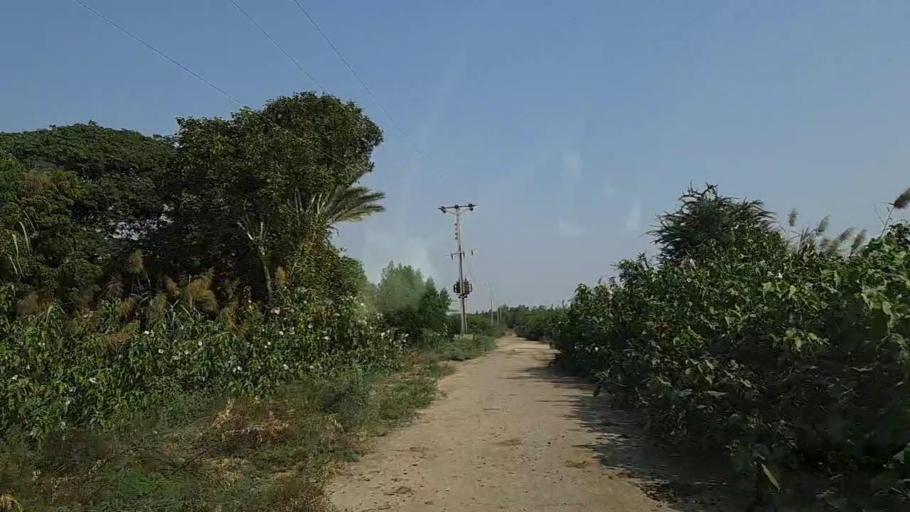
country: PK
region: Sindh
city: Mirpur Sakro
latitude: 24.6512
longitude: 67.6951
